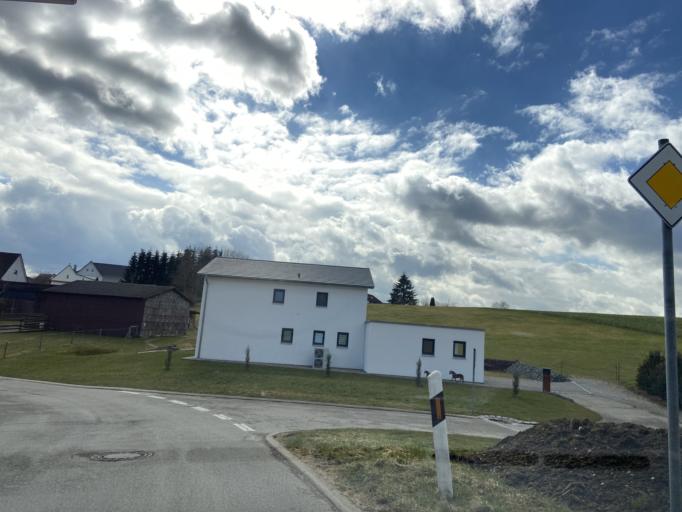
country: DE
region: Baden-Wuerttemberg
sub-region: Tuebingen Region
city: Mengen
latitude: 47.9849
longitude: 9.3174
